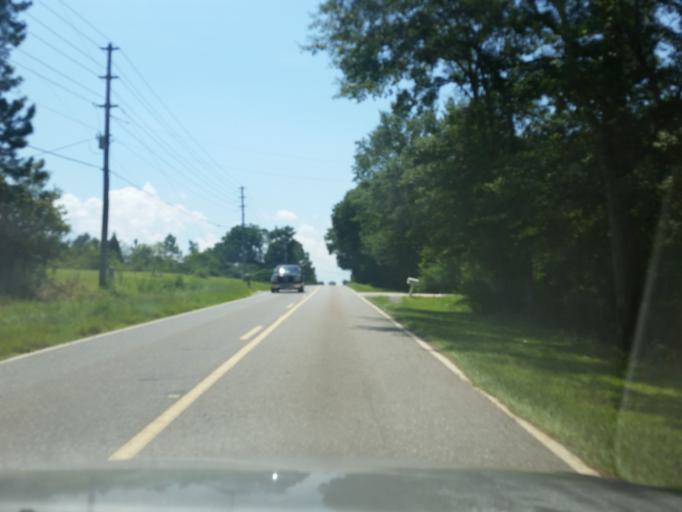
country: US
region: Alabama
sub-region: Baldwin County
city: Robertsdale
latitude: 30.6260
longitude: -87.6472
